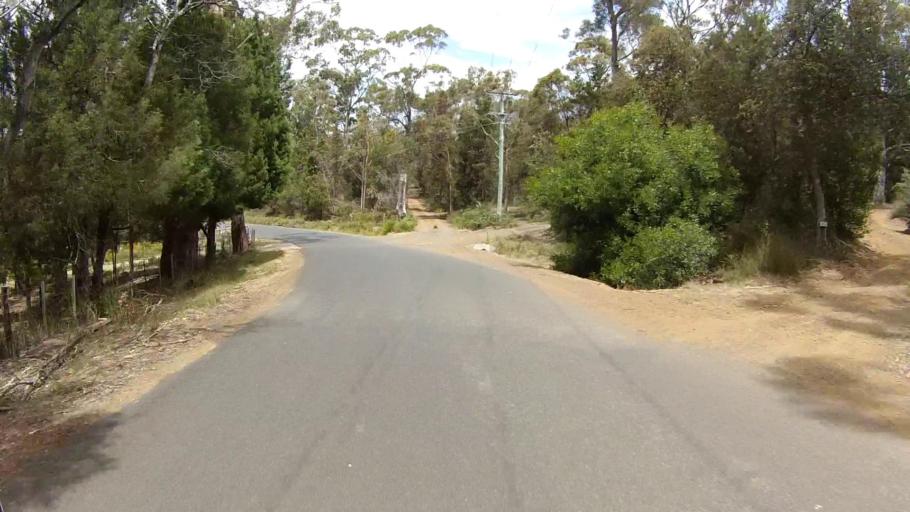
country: AU
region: Tasmania
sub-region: Sorell
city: Sorell
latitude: -42.5898
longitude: 147.9147
